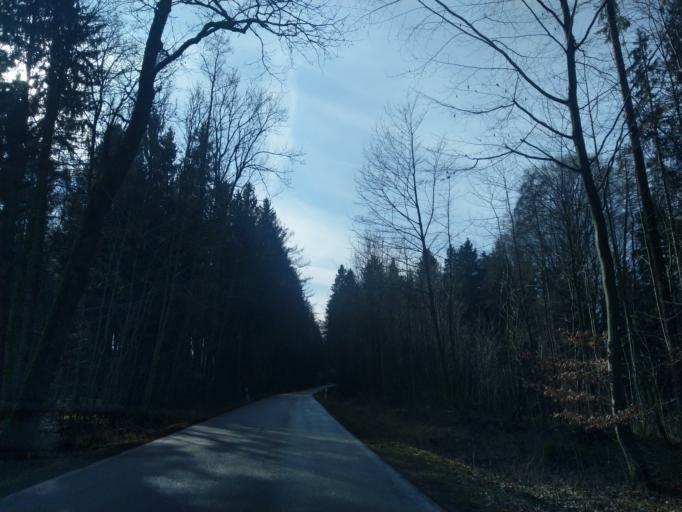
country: DE
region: Bavaria
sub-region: Lower Bavaria
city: Buchhofen
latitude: 48.6635
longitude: 12.9181
